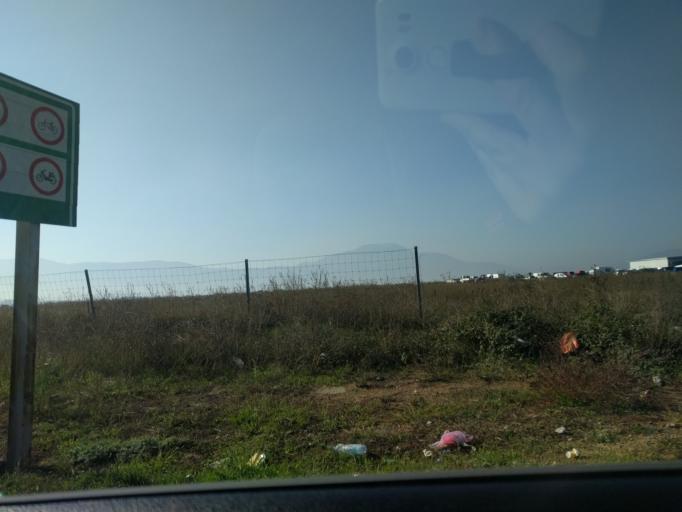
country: XK
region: Prizren
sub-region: Prizren
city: Prizren
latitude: 42.2508
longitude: 20.7085
